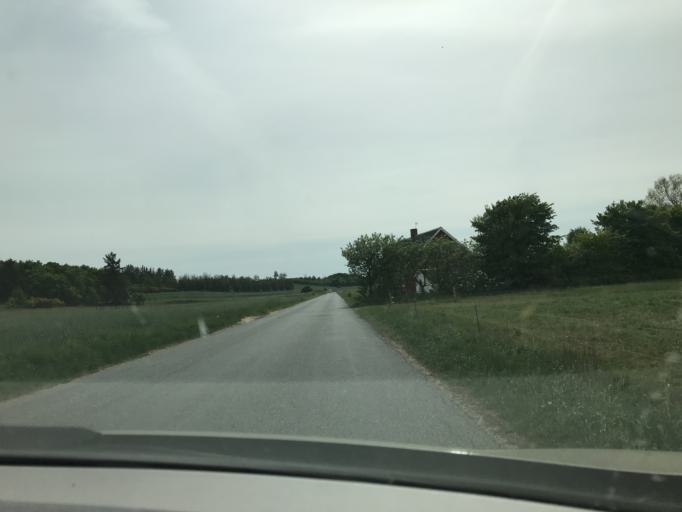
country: DK
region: Central Jutland
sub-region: Norddjurs Kommune
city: Allingabro
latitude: 56.5881
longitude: 10.3115
